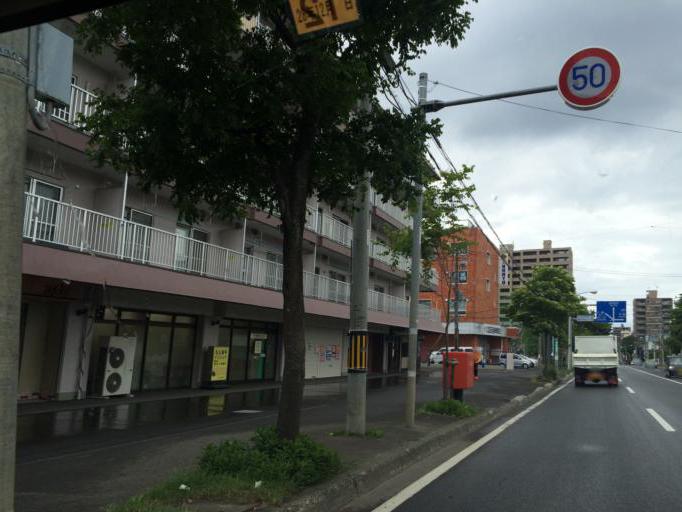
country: JP
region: Hokkaido
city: Sapporo
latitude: 43.0288
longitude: 141.3379
